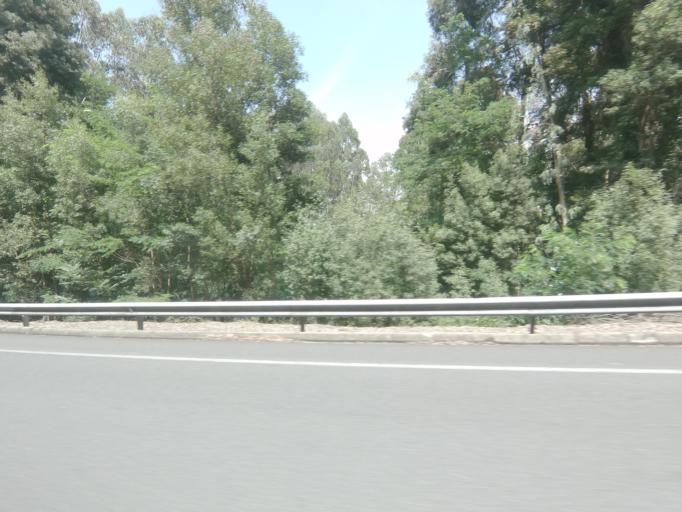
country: ES
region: Galicia
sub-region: Provincia de Pontevedra
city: Gondomar
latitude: 42.0956
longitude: -8.7580
